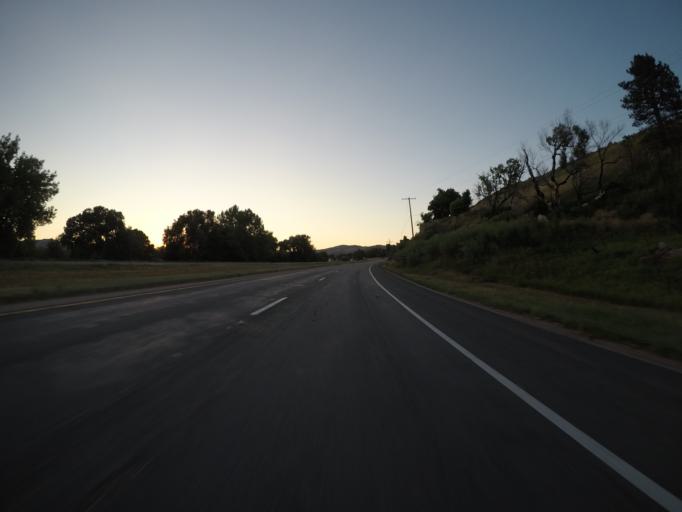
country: US
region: Colorado
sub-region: Larimer County
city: Laporte
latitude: 40.6556
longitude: -105.1809
